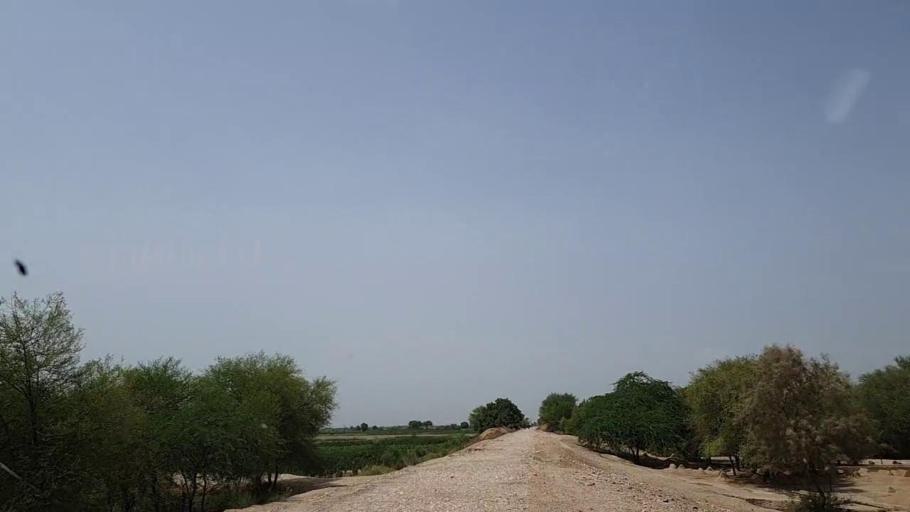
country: PK
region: Sindh
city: Tharu Shah
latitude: 27.0349
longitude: 68.1117
